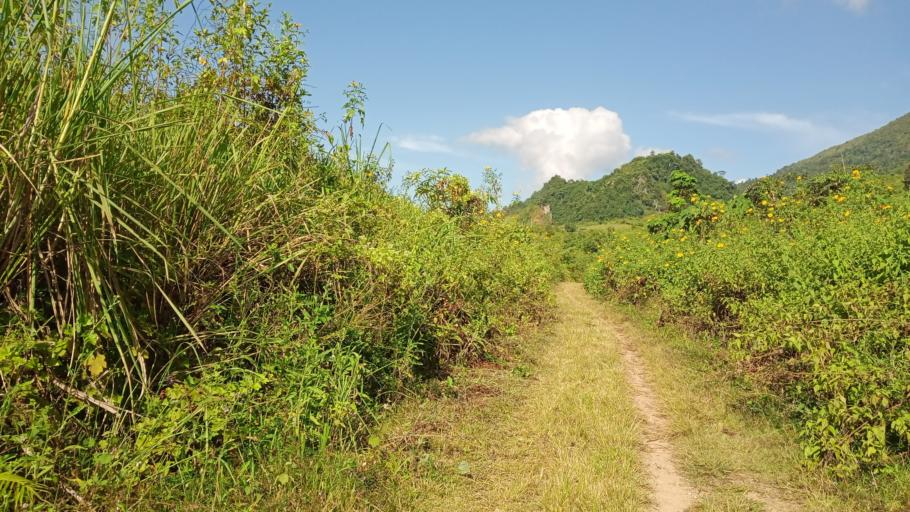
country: LA
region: Xiangkhoang
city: Phonsavan
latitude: 19.1098
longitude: 102.9302
